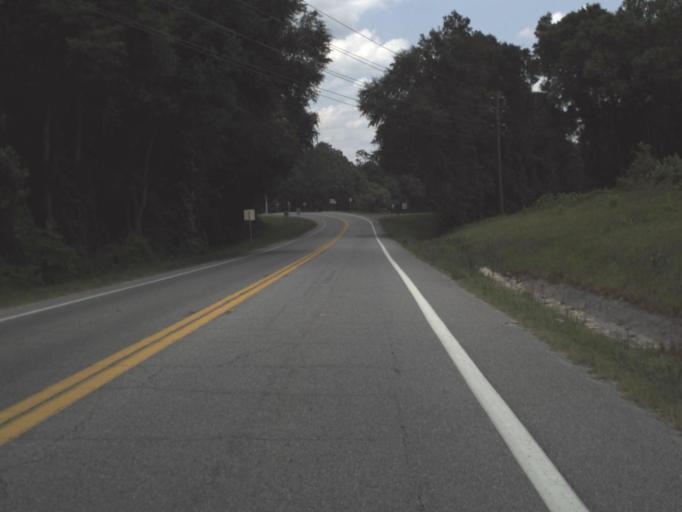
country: US
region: Florida
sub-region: Hamilton County
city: Jasper
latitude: 30.5288
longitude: -83.0449
